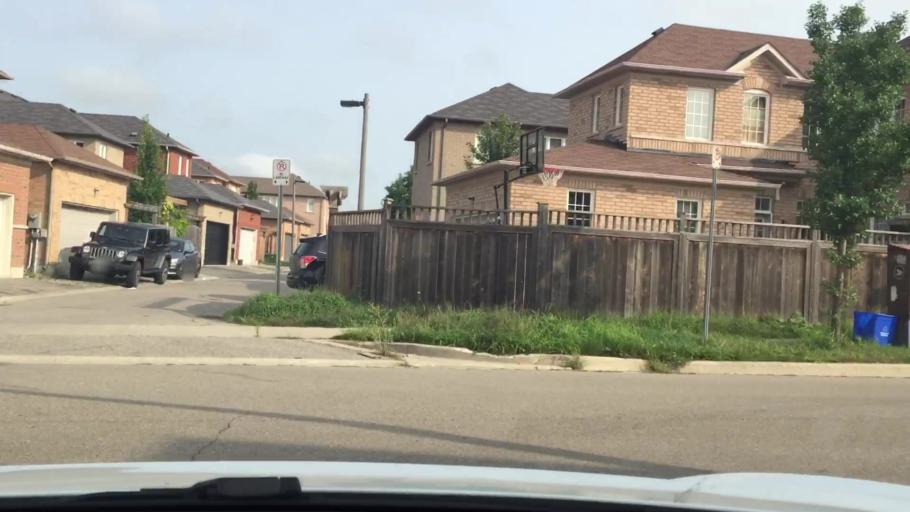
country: CA
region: Ontario
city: Markham
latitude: 43.8984
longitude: -79.2197
